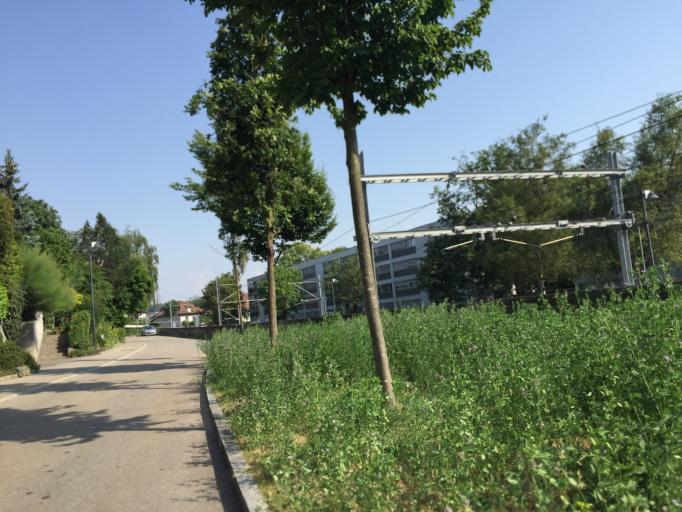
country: CH
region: Bern
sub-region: Bern-Mittelland District
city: Zollikofen
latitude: 46.9796
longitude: 7.4614
